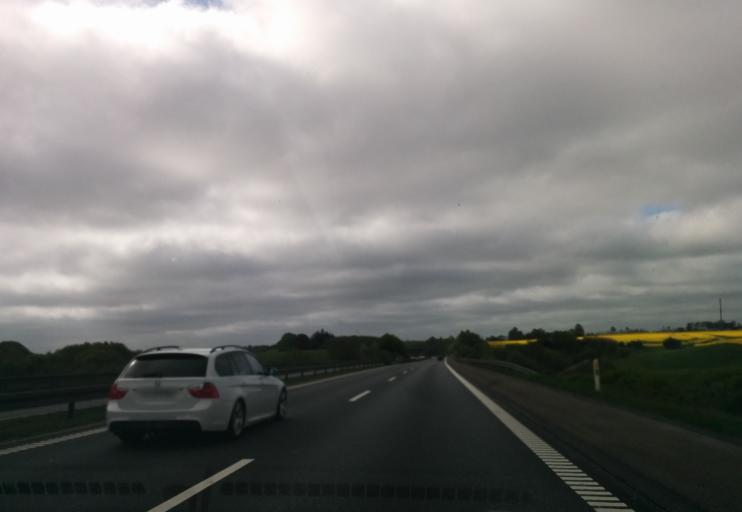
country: DK
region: South Denmark
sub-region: Fredericia Kommune
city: Taulov
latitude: 55.5737
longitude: 9.6151
